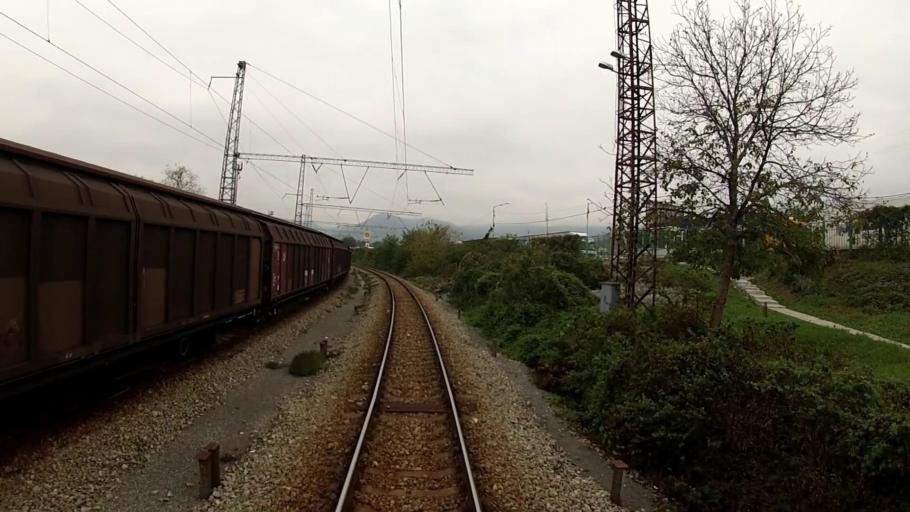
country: RS
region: Central Serbia
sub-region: Pirotski Okrug
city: Dimitrovgrad
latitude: 42.9939
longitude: 22.8446
